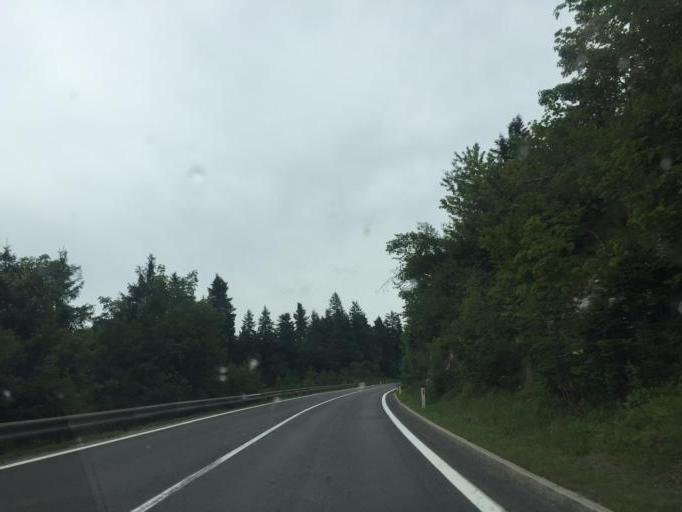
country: SI
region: Logatec
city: Logatec
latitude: 45.9126
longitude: 14.2426
